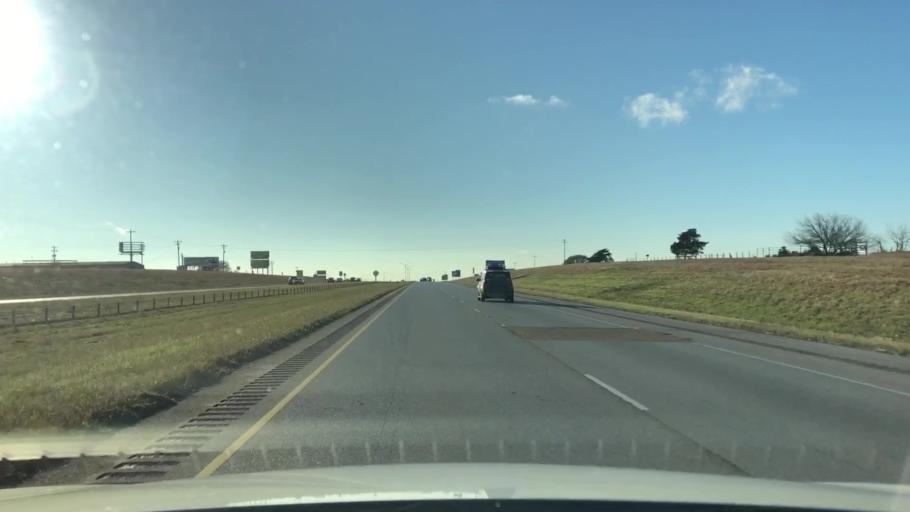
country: US
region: Texas
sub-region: Fayette County
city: Schulenburg
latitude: 29.6956
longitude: -96.8899
